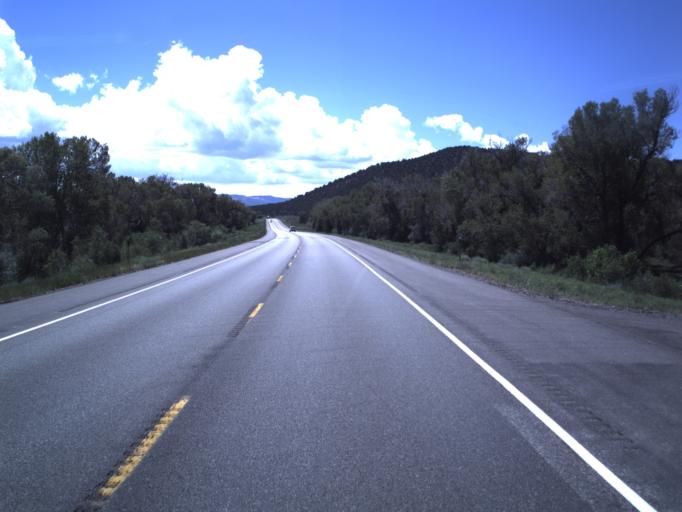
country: US
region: Utah
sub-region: Garfield County
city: Panguitch
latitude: 37.8044
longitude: -112.4010
